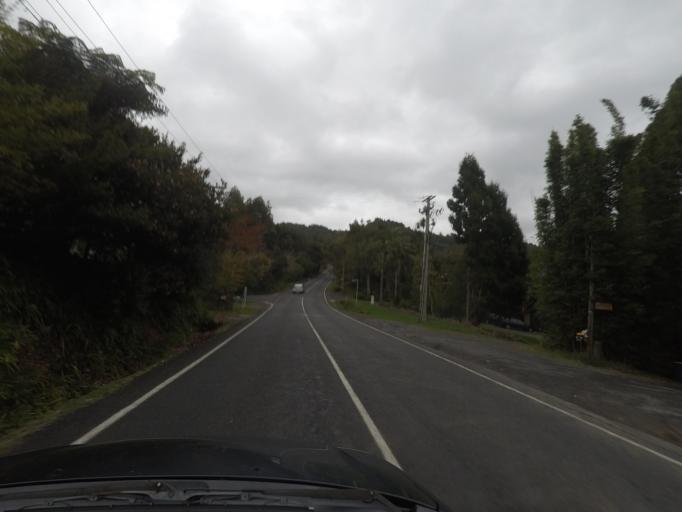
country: NZ
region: Auckland
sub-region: Auckland
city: Titirangi
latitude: -36.9302
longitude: 174.5931
